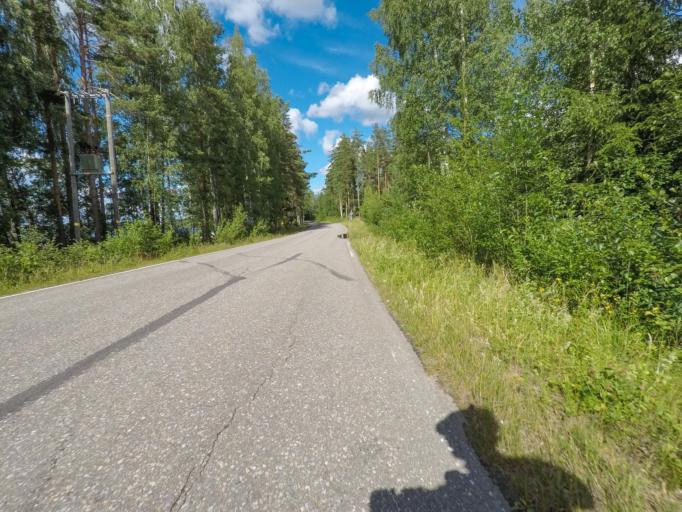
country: FI
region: South Karelia
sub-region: Lappeenranta
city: Joutseno
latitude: 61.1162
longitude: 28.3740
